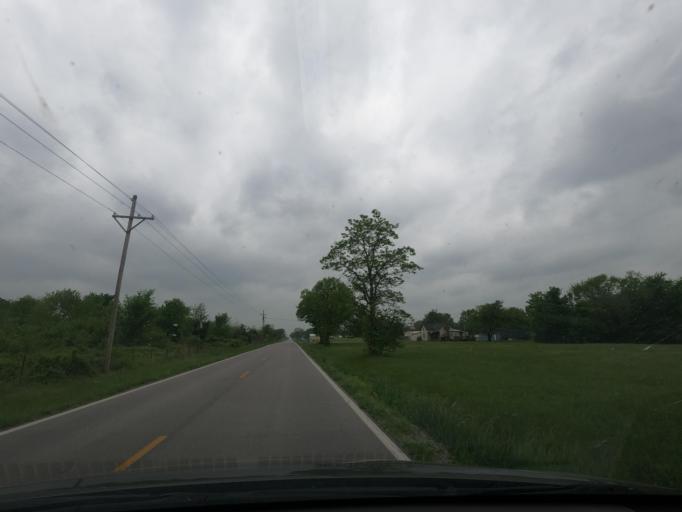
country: US
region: Kansas
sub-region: Cherokee County
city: Columbus
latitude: 37.2817
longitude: -94.9172
